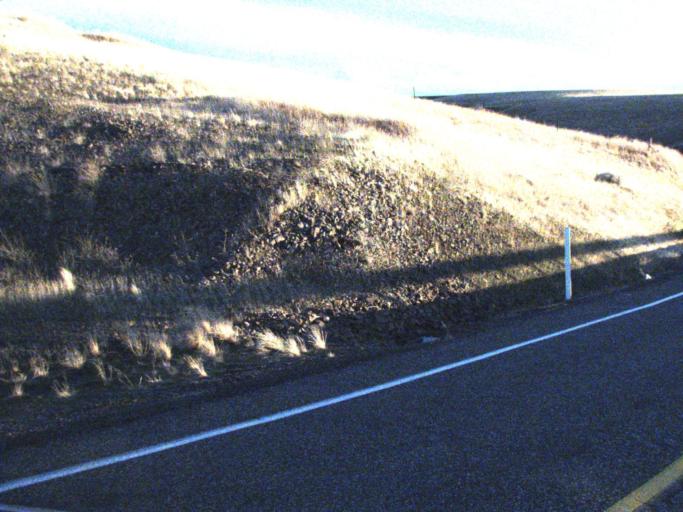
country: US
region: Washington
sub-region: Garfield County
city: Pomeroy
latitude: 46.5283
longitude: -117.7867
